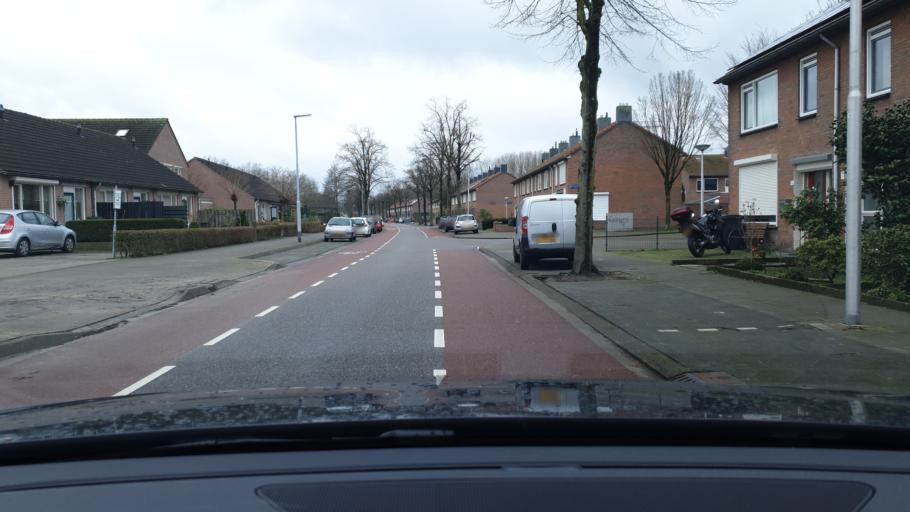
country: NL
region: North Brabant
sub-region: Gemeente Eindhoven
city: Eindhoven
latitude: 51.4273
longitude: 5.4528
